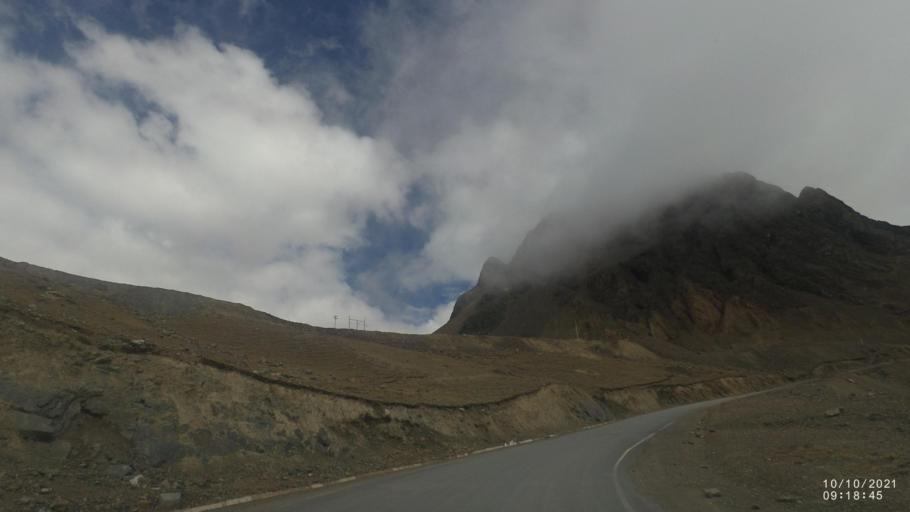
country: BO
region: La Paz
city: Quime
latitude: -17.0542
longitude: -67.2985
